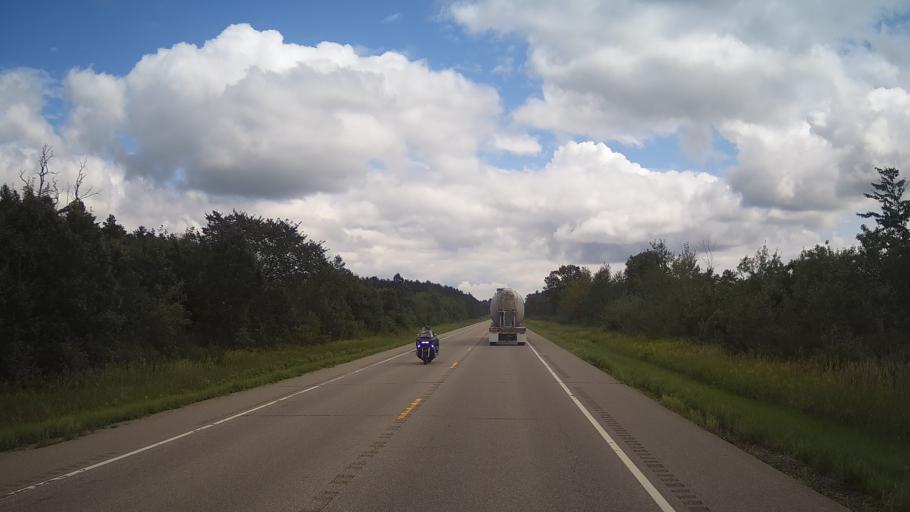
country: US
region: Wisconsin
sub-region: Marquette County
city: Westfield
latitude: 44.0220
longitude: -89.6280
